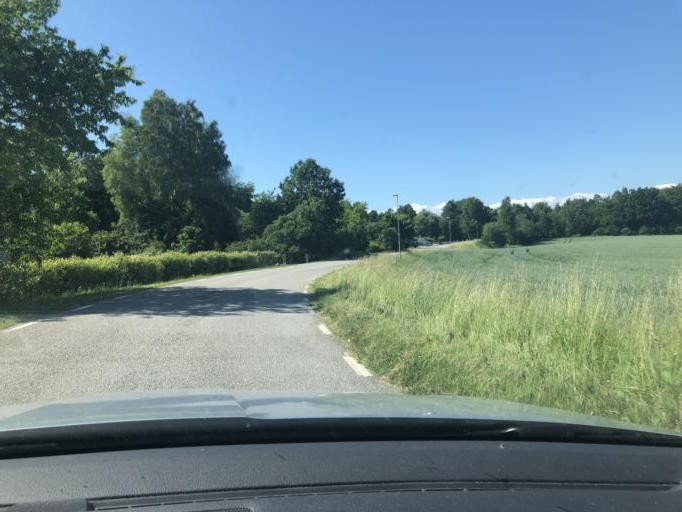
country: SE
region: Blekinge
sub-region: Karlshamns Kommun
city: Morrum
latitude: 56.1775
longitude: 14.6773
